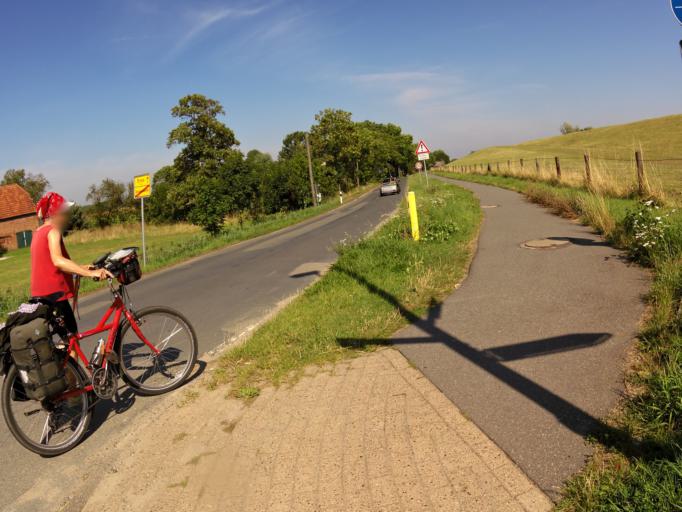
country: DE
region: Lower Saxony
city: Elsfleth
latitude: 53.2772
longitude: 8.4805
